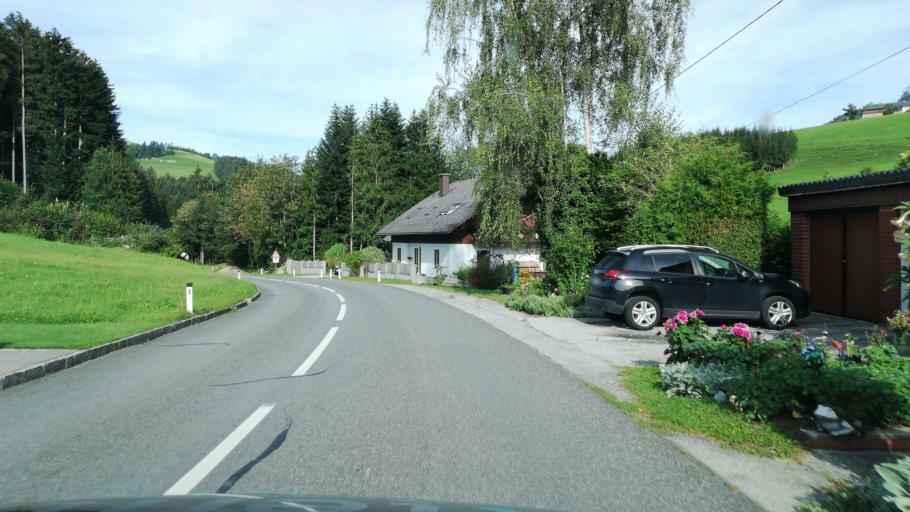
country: AT
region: Upper Austria
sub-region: Politischer Bezirk Steyr-Land
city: Maria Neustift
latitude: 47.9482
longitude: 14.6116
